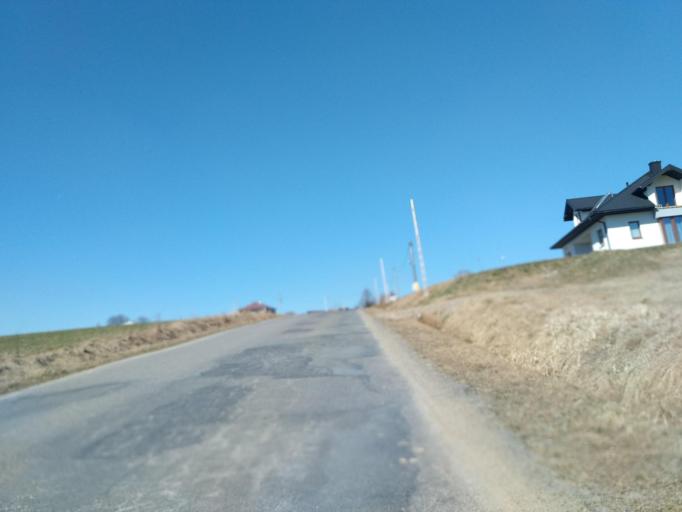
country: PL
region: Subcarpathian Voivodeship
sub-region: Powiat debicki
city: Brzostek
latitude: 49.9429
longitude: 21.4347
